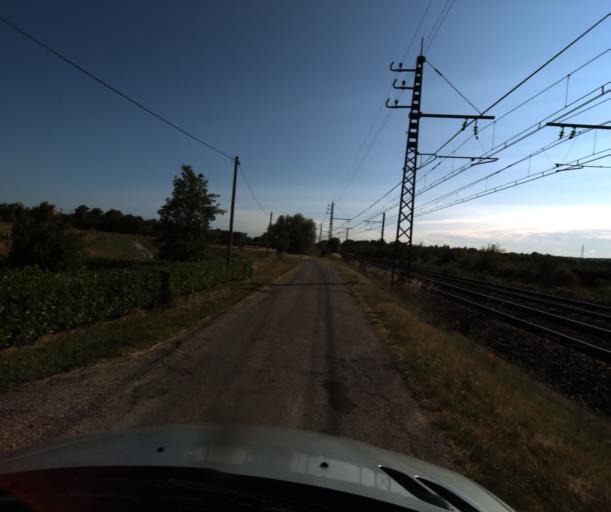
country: FR
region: Midi-Pyrenees
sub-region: Departement du Tarn-et-Garonne
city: Bressols
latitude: 43.9712
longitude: 1.3108
